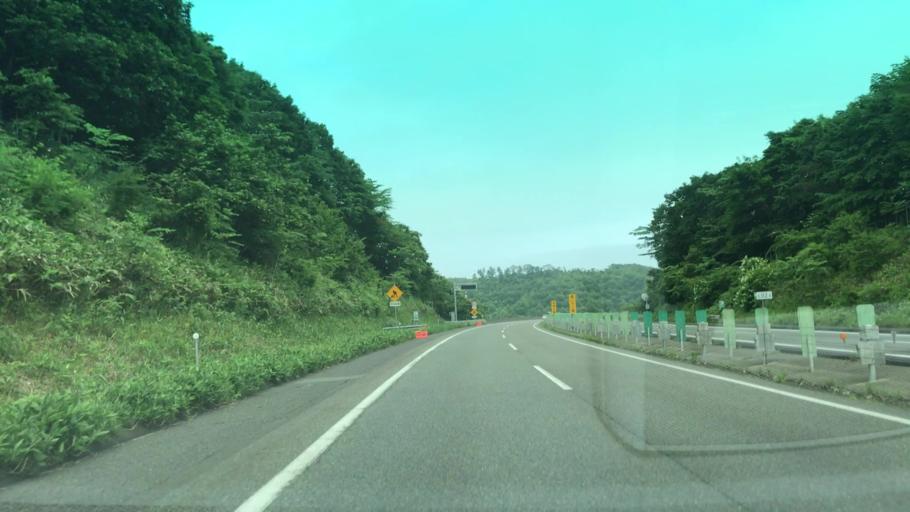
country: JP
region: Hokkaido
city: Shiraoi
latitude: 42.4932
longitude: 141.2410
